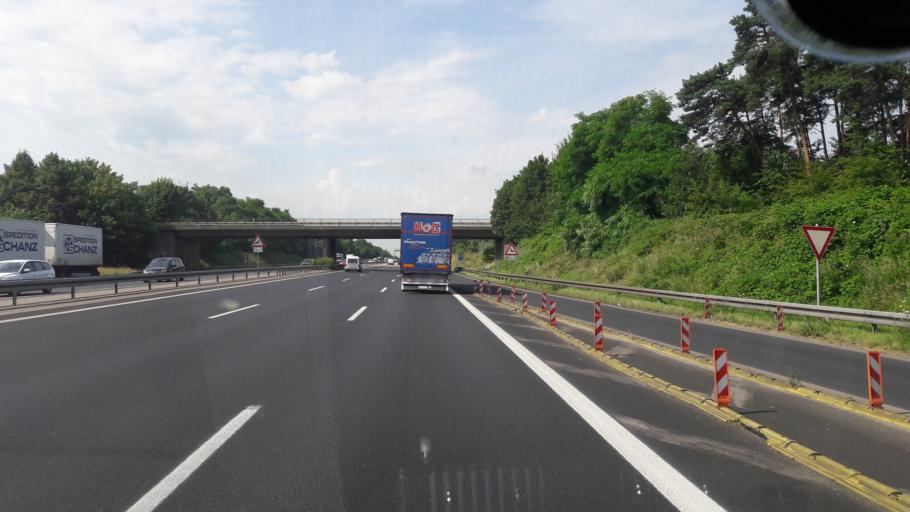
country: DE
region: Baden-Wuerttemberg
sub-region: Karlsruhe Region
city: Iffezheim
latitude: 48.8080
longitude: 8.1817
